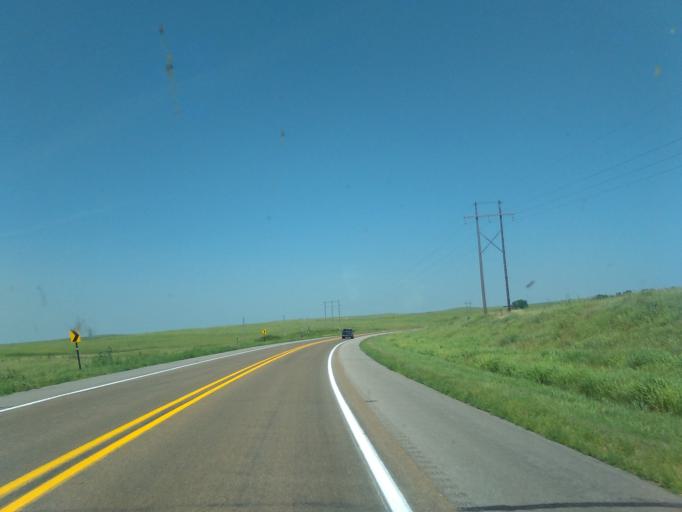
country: US
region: Nebraska
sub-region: Lincoln County
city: North Platte
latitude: 40.7839
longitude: -100.7526
